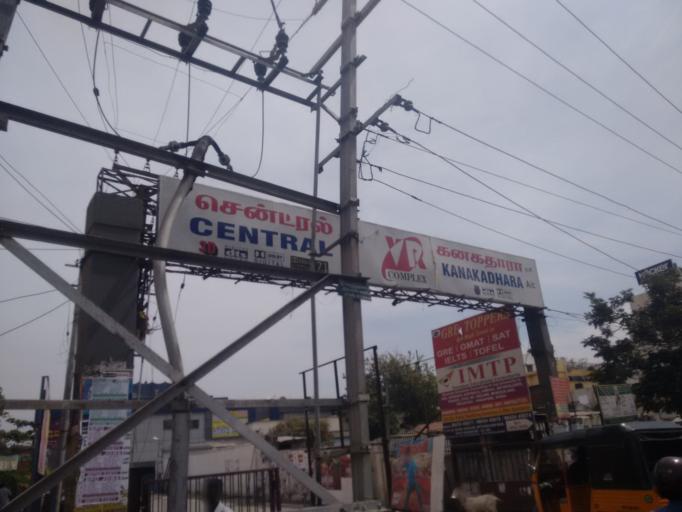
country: IN
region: Tamil Nadu
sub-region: Coimbatore
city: Coimbatore
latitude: 11.0159
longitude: 76.9546
